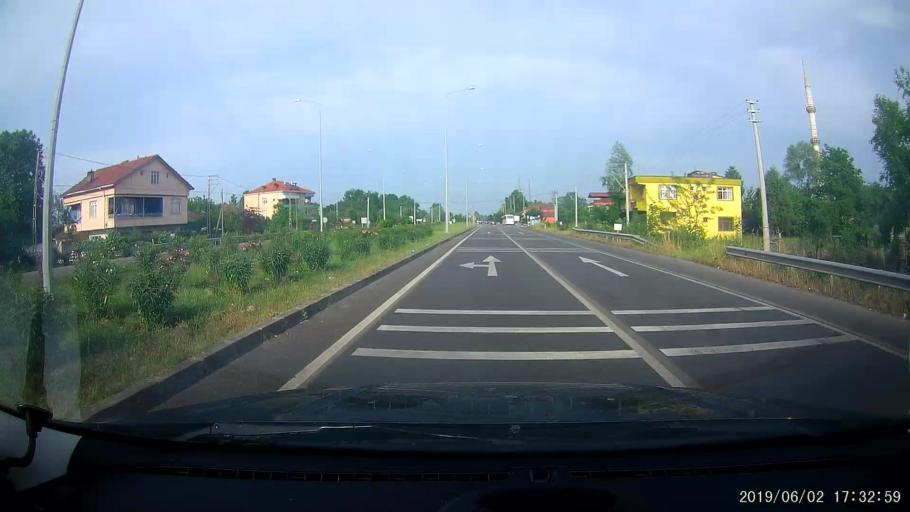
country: TR
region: Samsun
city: Carsamba
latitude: 41.2206
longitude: 36.8388
